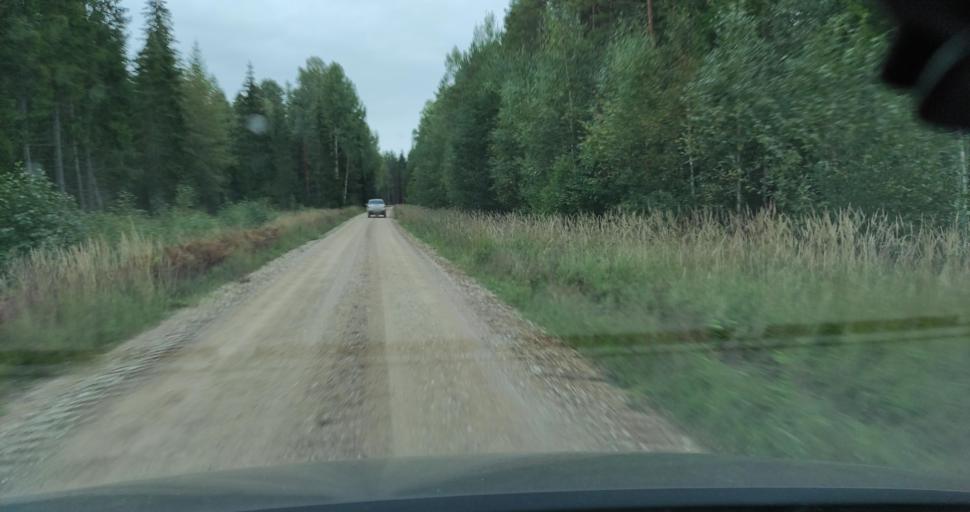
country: LV
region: Talsu Rajons
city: Stende
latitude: 57.0237
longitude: 22.3552
